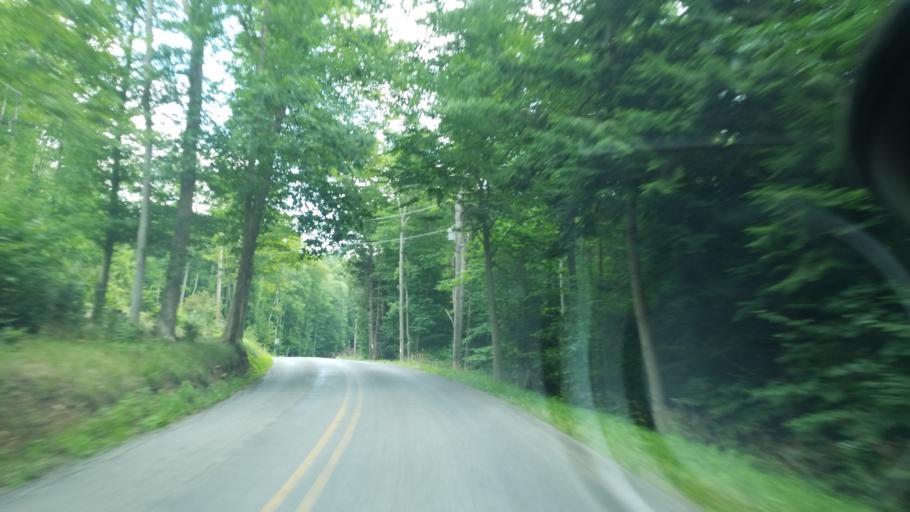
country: US
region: Pennsylvania
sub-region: Jefferson County
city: Brookville
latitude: 41.2307
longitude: -79.0611
